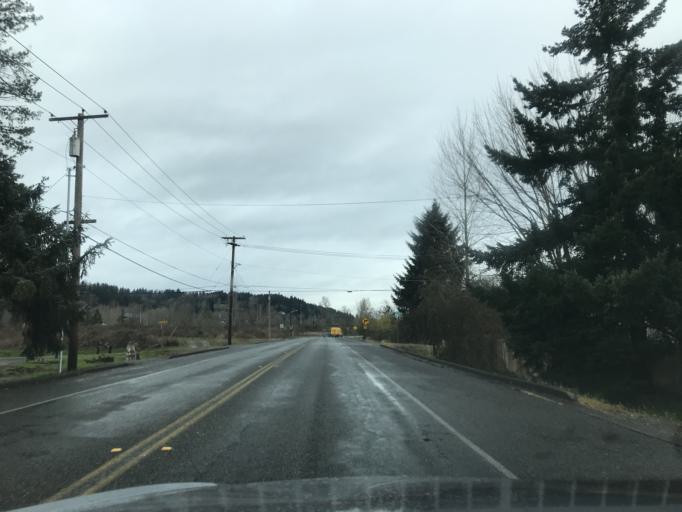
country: US
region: Washington
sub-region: King County
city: Algona
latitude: 47.2918
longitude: -122.2551
